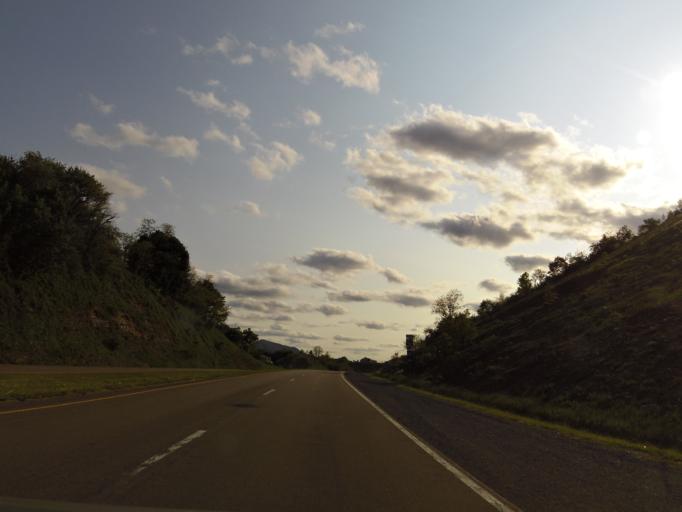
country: US
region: Virginia
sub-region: Tazewell County
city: Tazewell
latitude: 37.1312
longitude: -81.5187
